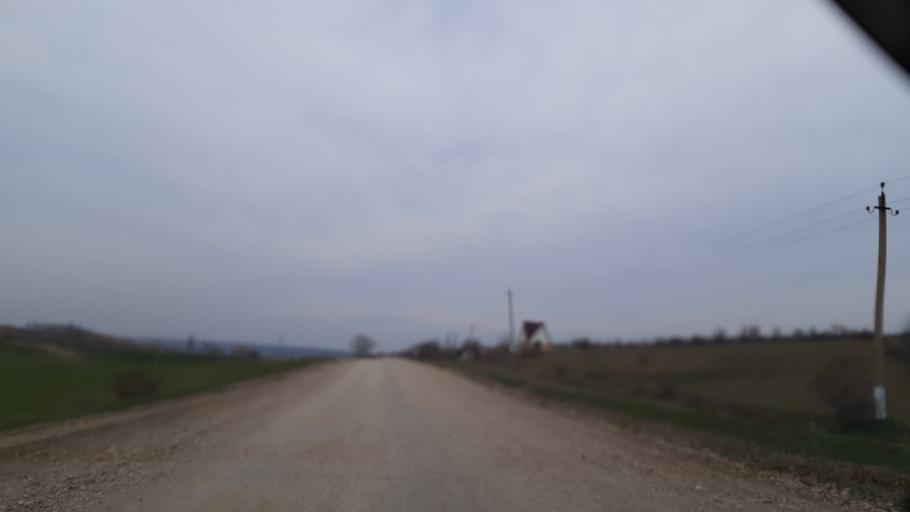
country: MD
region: Soldanesti
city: Soldanesti
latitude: 47.6304
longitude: 28.6597
